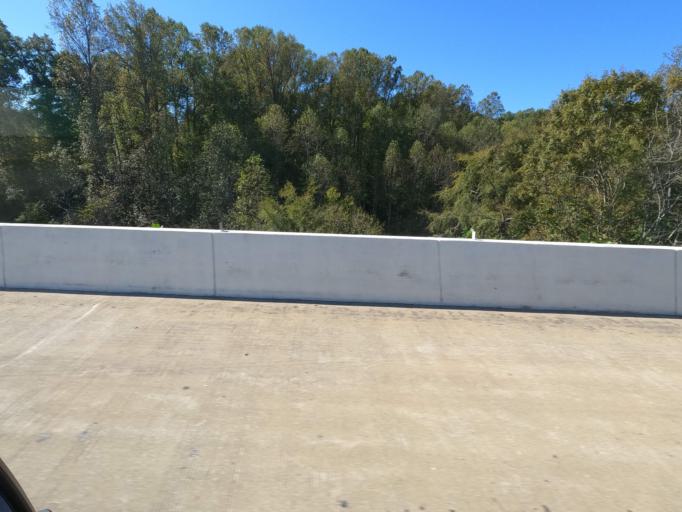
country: US
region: Tennessee
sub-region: Maury County
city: Spring Hill
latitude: 35.8183
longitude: -87.0350
